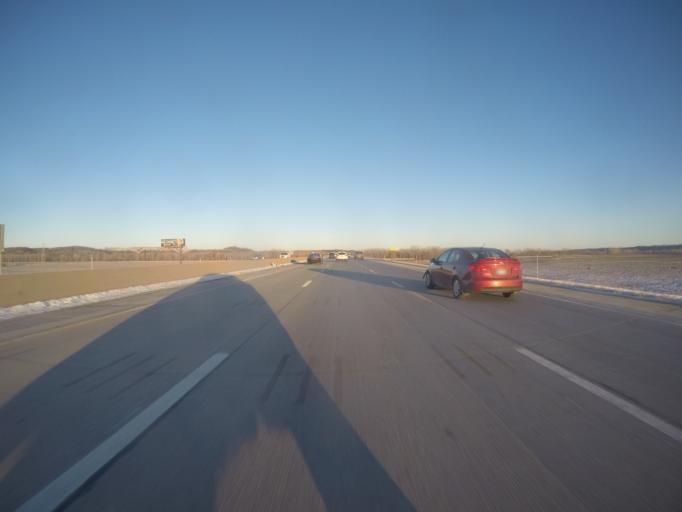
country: US
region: Missouri
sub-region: Platte County
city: Weatherby Lake
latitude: 39.1894
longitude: -94.7818
